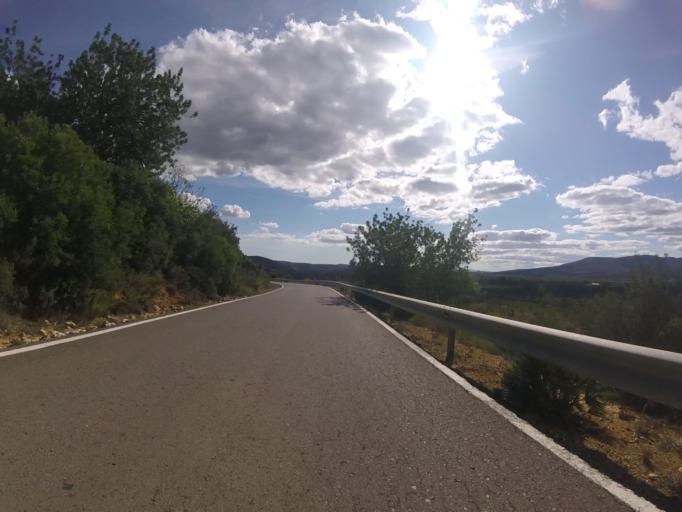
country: ES
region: Valencia
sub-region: Provincia de Castello
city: Cuevas de Vinroma
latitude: 40.3694
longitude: 0.1180
